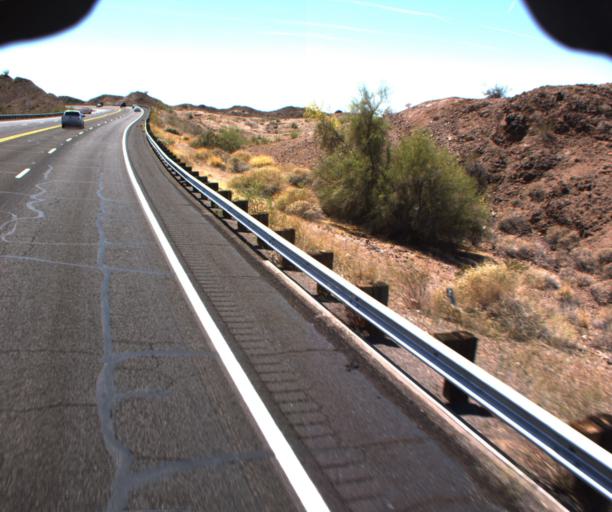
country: US
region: Arizona
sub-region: La Paz County
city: Cienega Springs
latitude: 34.2023
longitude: -114.2080
